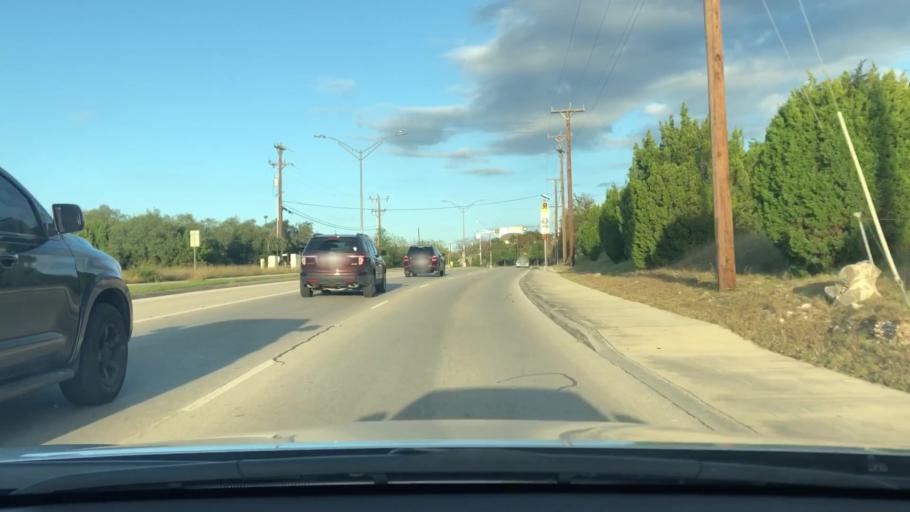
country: US
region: Texas
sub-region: Bexar County
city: Hollywood Park
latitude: 29.6353
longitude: -98.5109
